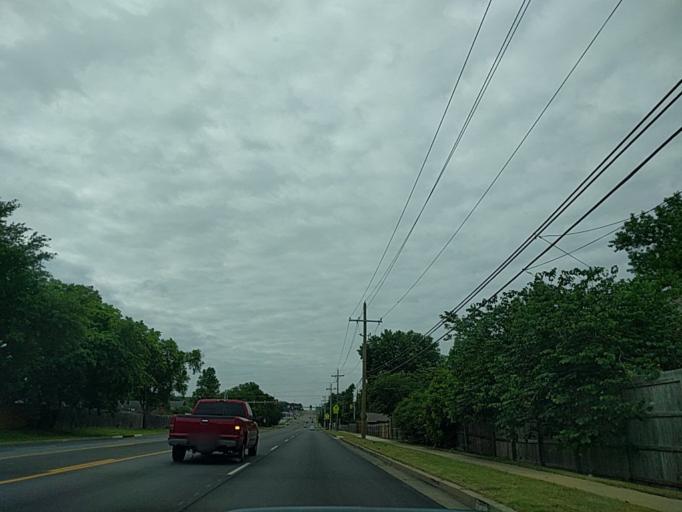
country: US
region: Oklahoma
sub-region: Tulsa County
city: Jenks
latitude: 36.0827
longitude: -95.9044
